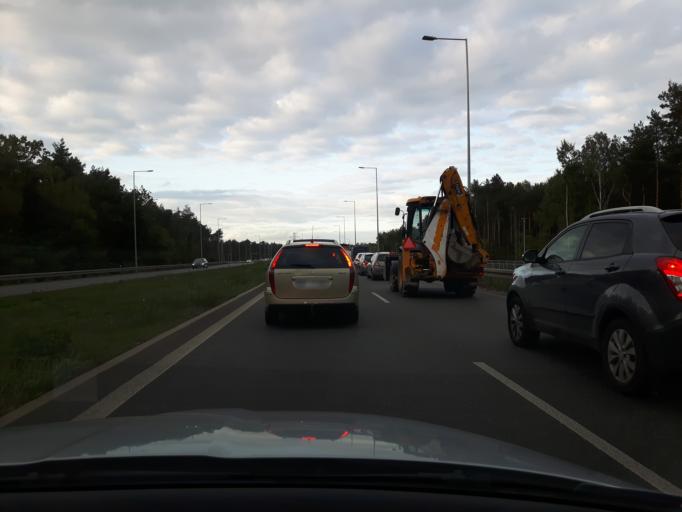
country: PL
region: Masovian Voivodeship
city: Zielonka
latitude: 52.2906
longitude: 21.1392
